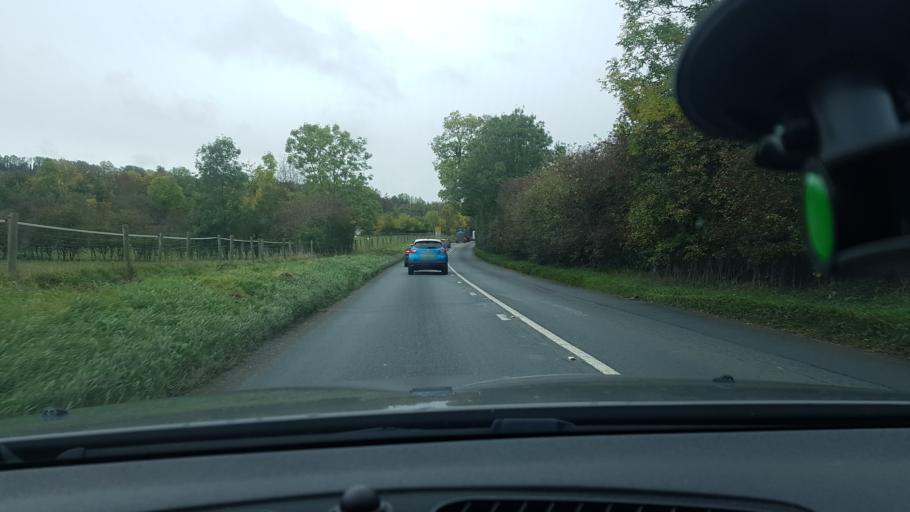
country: GB
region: England
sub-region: Wiltshire
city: Marlborough
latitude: 51.4504
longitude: -1.7245
